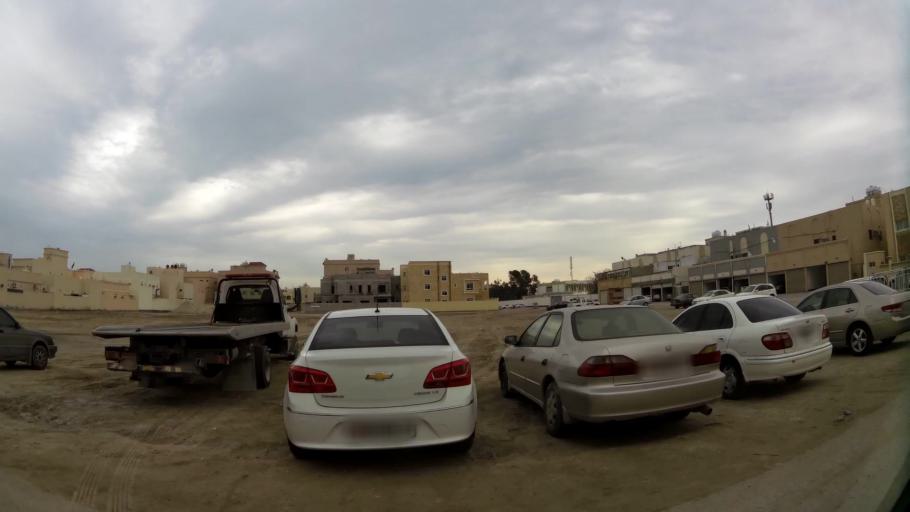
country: BH
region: Northern
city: Sitrah
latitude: 26.1705
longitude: 50.6058
